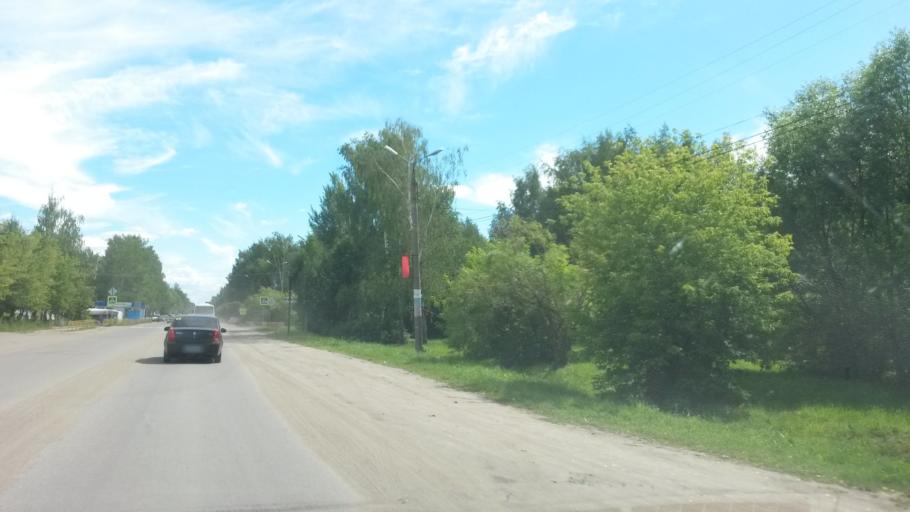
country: RU
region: Ivanovo
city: Zavolzhsk
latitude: 57.4908
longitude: 42.1383
